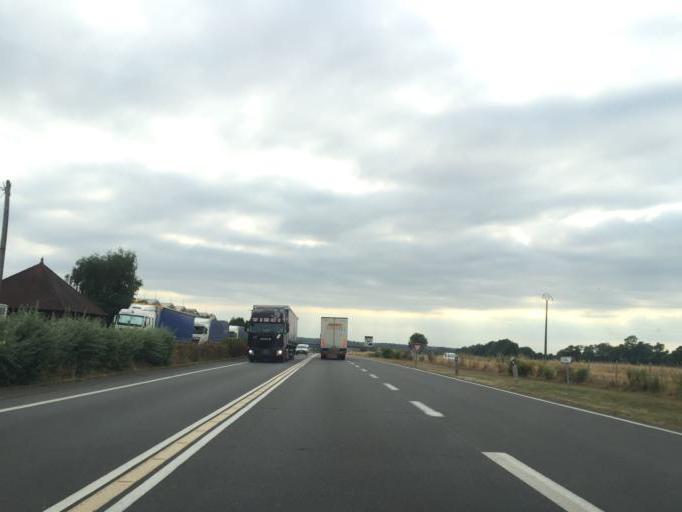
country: FR
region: Auvergne
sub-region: Departement de l'Allier
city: Beaulon
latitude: 46.5345
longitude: 3.5893
